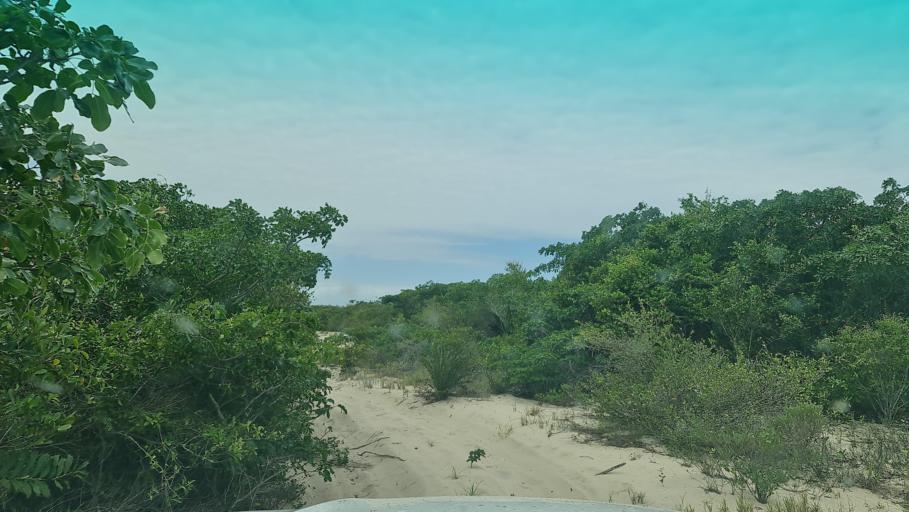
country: MZ
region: Maputo
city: Manhica
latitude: -25.6367
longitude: 32.7846
